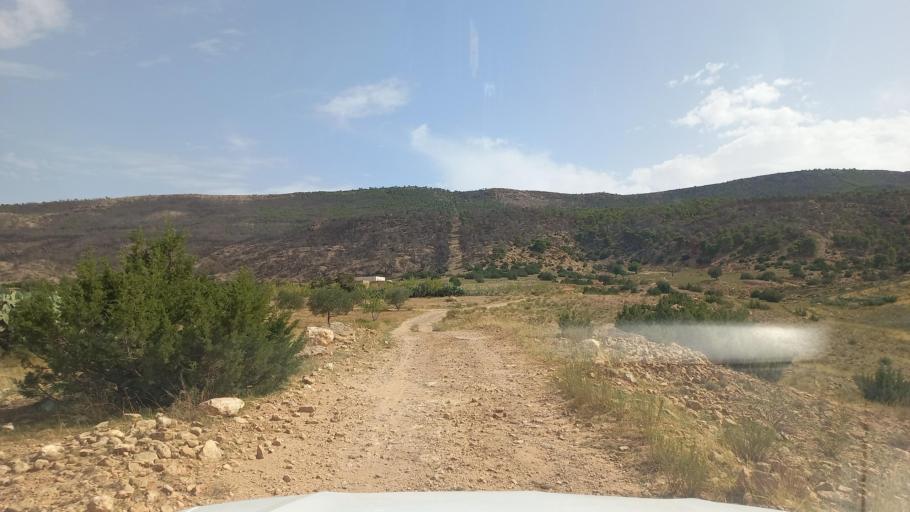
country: TN
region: Al Qasrayn
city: Kasserine
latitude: 35.3560
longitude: 8.8892
